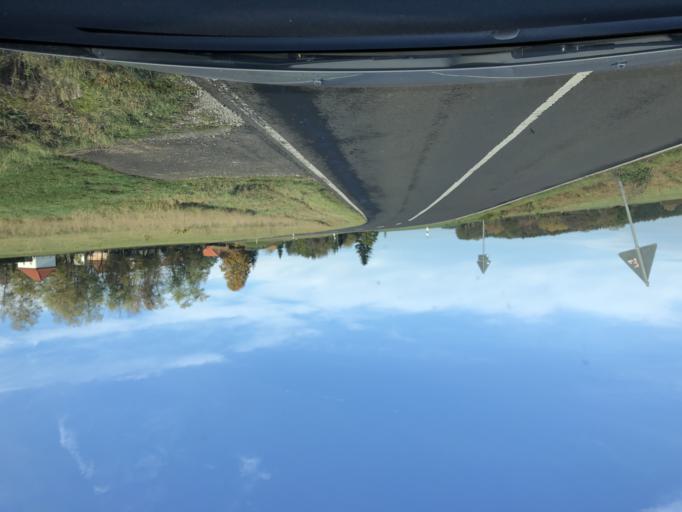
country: DE
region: Thuringia
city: Reurieth
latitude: 50.4649
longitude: 10.6579
